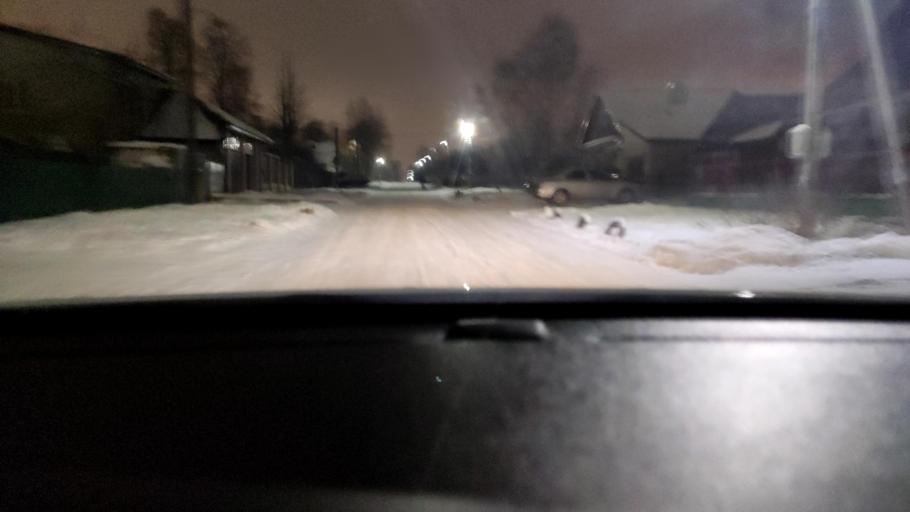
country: RU
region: Tatarstan
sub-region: Gorod Kazan'
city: Kazan
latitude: 55.8685
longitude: 49.0602
